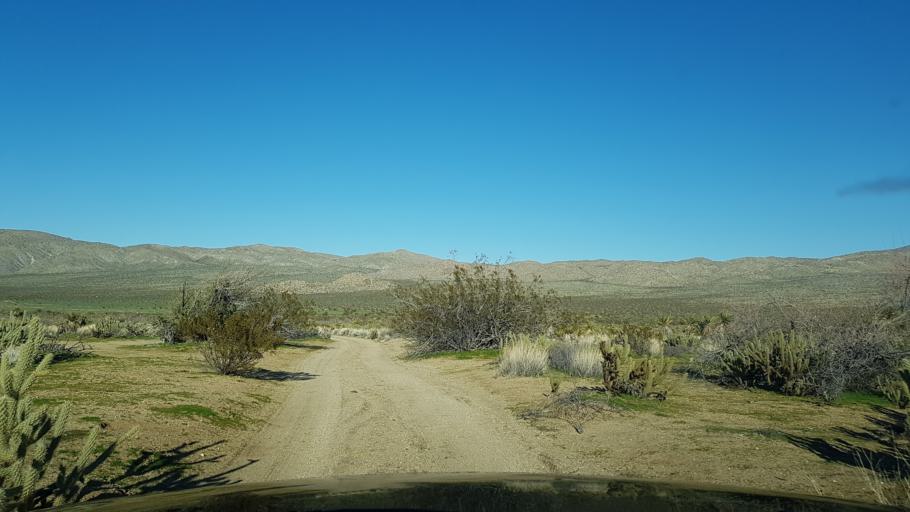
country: US
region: California
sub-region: San Diego County
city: Julian
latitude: 33.0520
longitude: -116.4240
